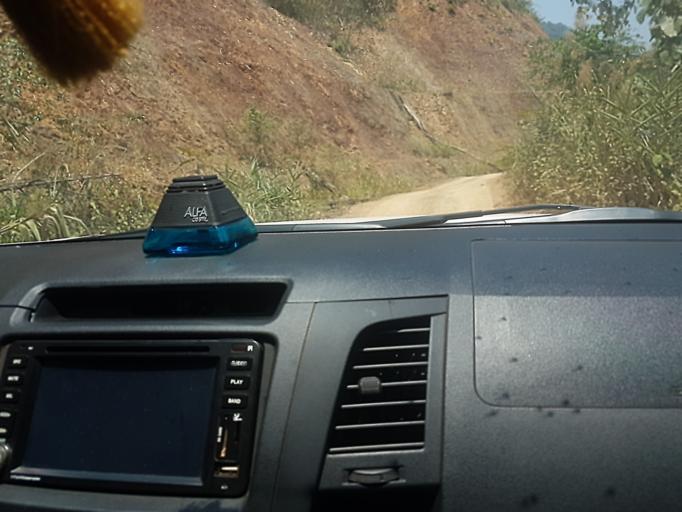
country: VN
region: Nghe An
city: Con Cuong
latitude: 18.6080
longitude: 104.7347
